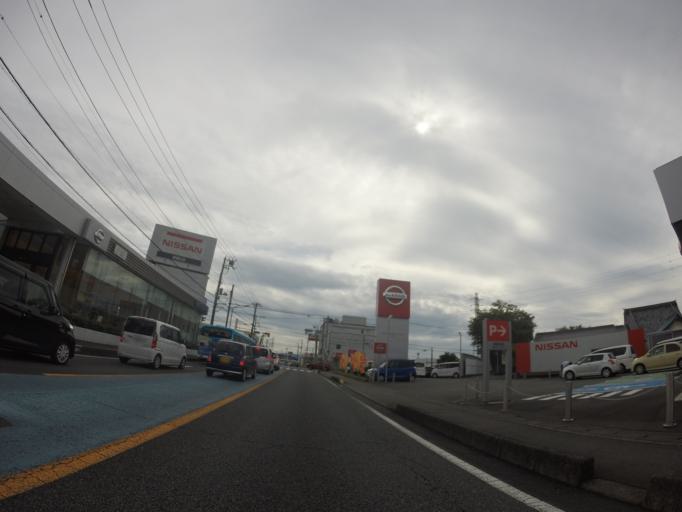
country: JP
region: Shizuoka
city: Fuji
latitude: 35.1881
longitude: 138.6528
